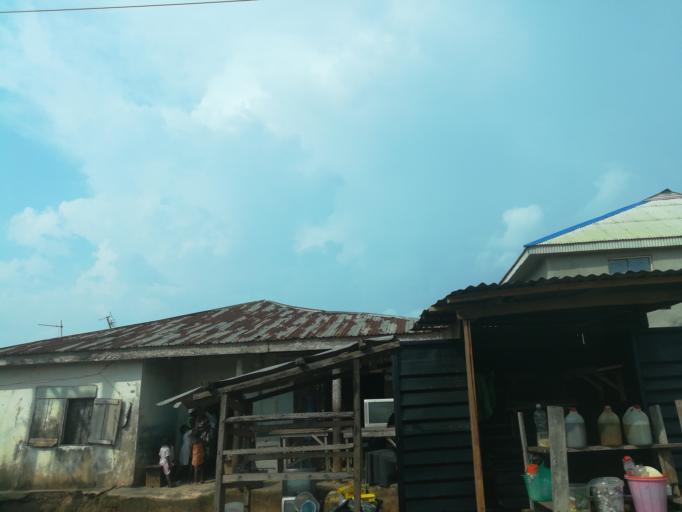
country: NG
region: Lagos
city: Ikorodu
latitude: 6.6640
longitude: 3.6740
